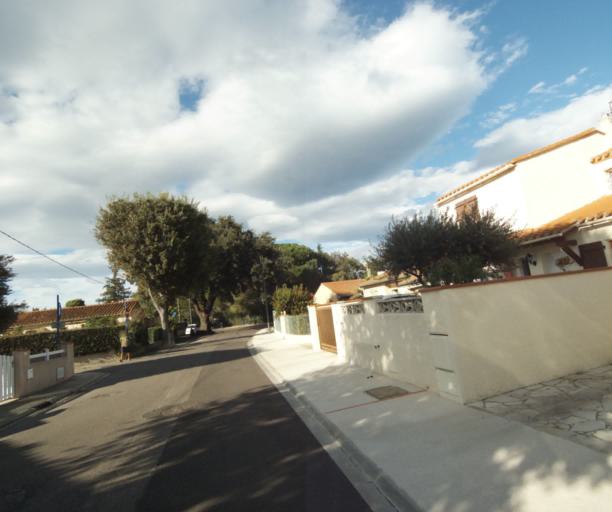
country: FR
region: Languedoc-Roussillon
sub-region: Departement des Pyrenees-Orientales
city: Argelers
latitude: 42.5445
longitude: 3.0309
